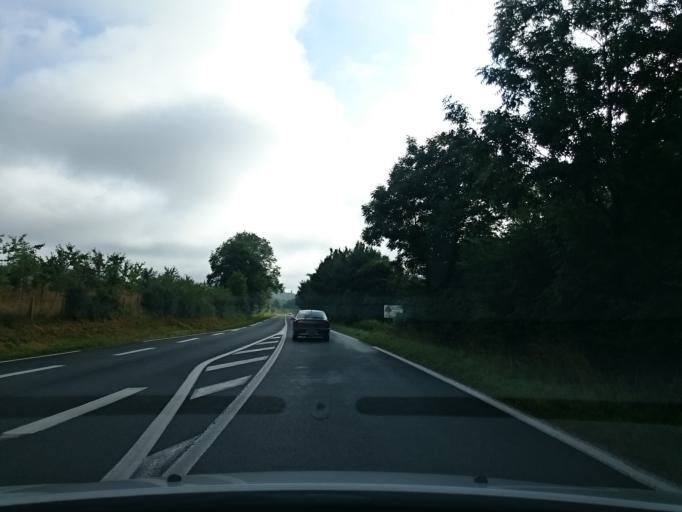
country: FR
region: Lower Normandy
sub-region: Departement du Calvados
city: Cambremer
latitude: 49.1153
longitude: 0.0551
